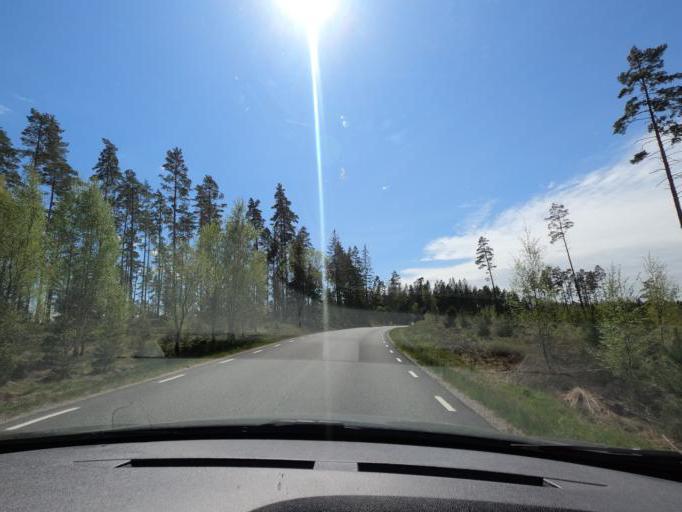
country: SE
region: Joenkoeping
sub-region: Varnamo Kommun
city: Bredaryd
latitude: 57.1564
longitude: 13.7359
